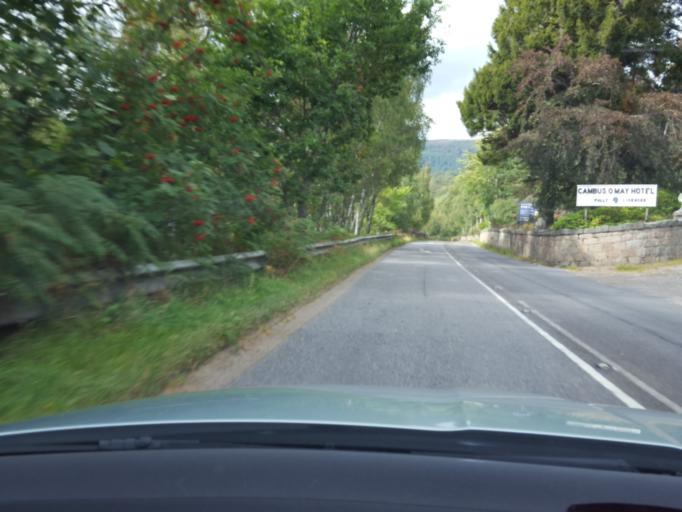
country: GB
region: Scotland
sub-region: Aberdeenshire
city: Ballater
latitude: 57.0655
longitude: -2.9555
